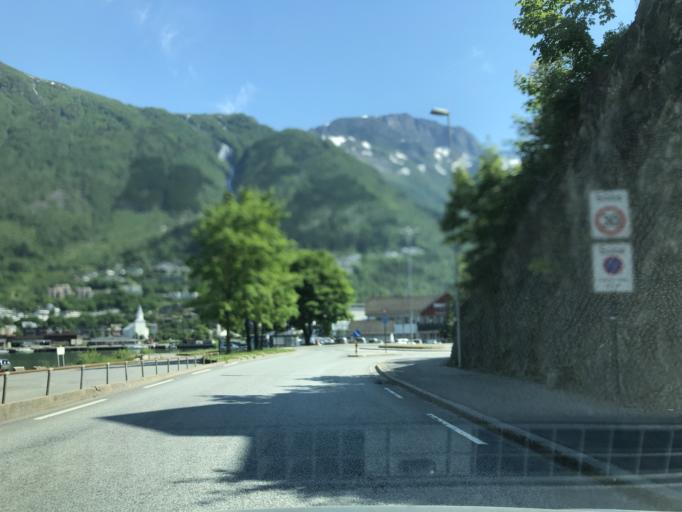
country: NO
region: Hordaland
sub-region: Odda
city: Odda
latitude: 60.0712
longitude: 6.5401
